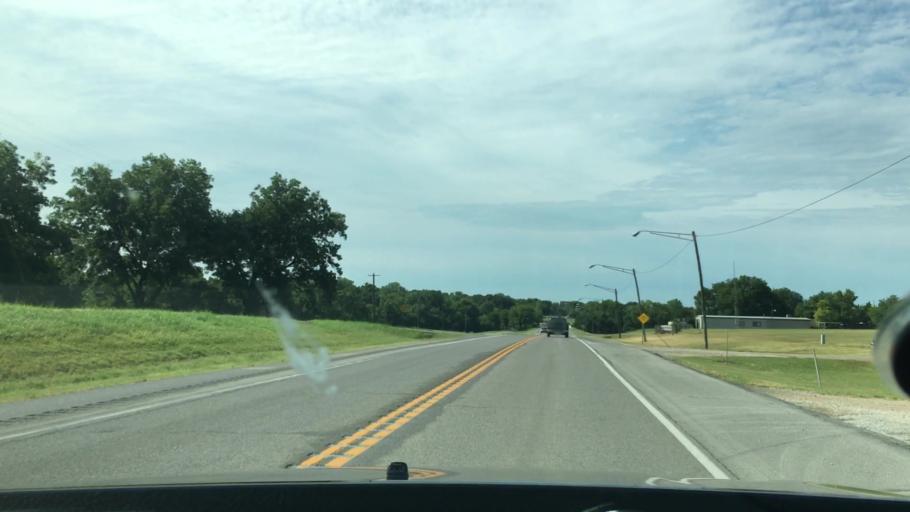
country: US
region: Oklahoma
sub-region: Murray County
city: Sulphur
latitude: 34.5201
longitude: -96.9689
